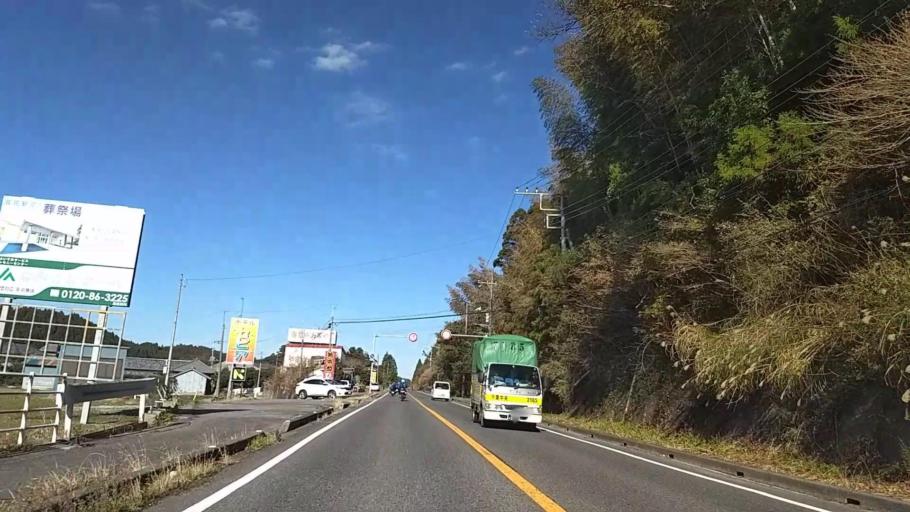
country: JP
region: Chiba
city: Ohara
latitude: 35.2064
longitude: 140.3745
